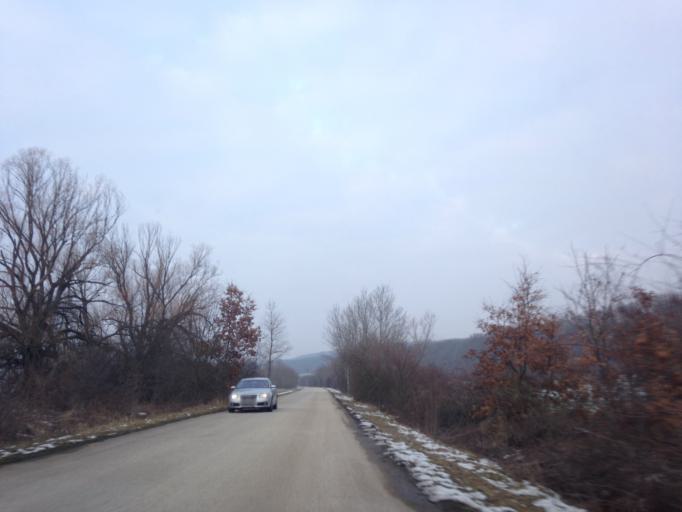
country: SK
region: Nitriansky
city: Surany
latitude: 48.0546
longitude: 18.3710
